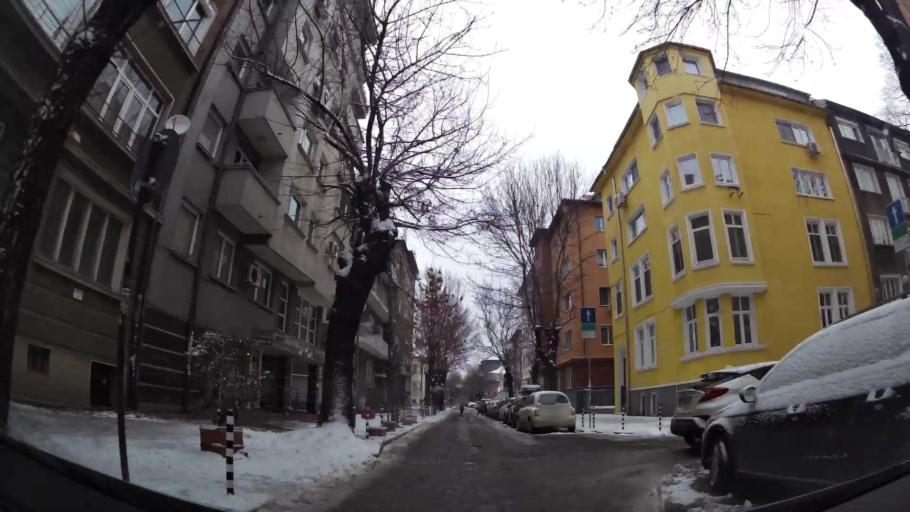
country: BG
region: Sofia-Capital
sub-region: Stolichna Obshtina
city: Sofia
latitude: 42.6937
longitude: 23.3440
